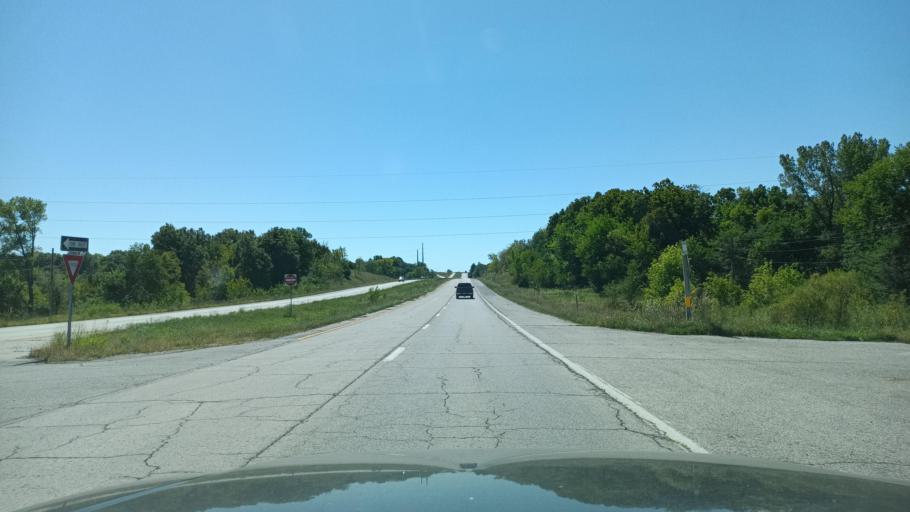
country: US
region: Missouri
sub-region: Adair County
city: Kirksville
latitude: 40.1521
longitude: -92.5722
